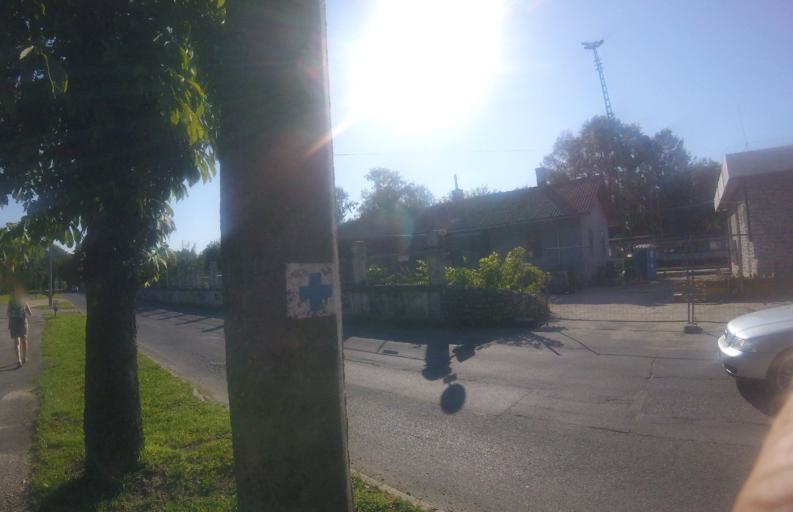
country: HU
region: Zala
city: Keszthely
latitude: 46.7583
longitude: 17.2472
